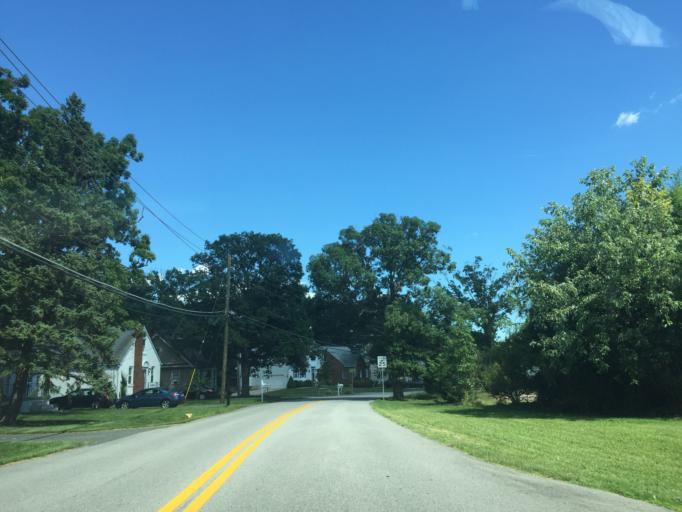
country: US
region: Maryland
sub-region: Baltimore County
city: Perry Hall
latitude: 39.4114
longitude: -76.4702
